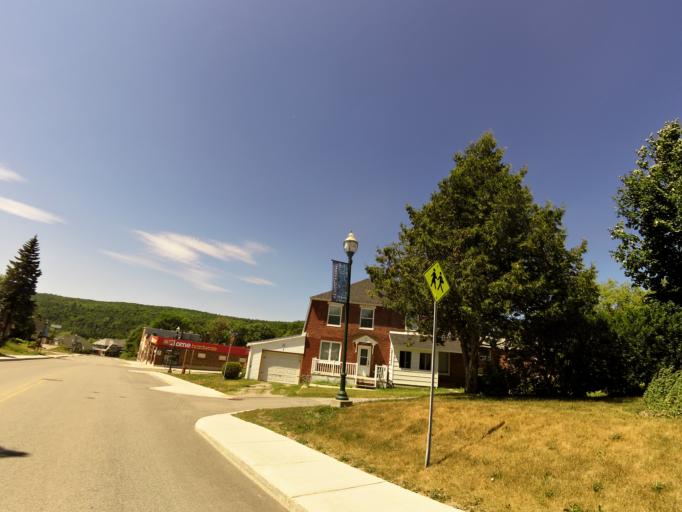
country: CA
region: Quebec
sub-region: Abitibi-Temiscamingue
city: Temiscaming
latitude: 46.7191
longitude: -79.0982
